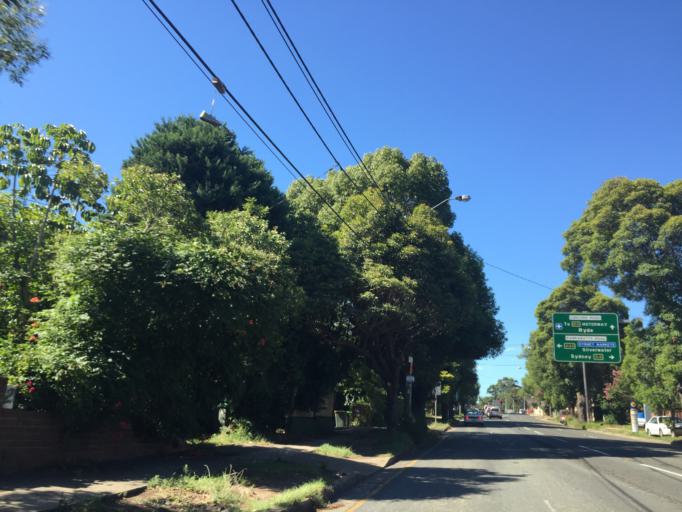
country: AU
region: New South Wales
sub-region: Strathfield
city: Homebush
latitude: -33.8684
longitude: 151.0928
